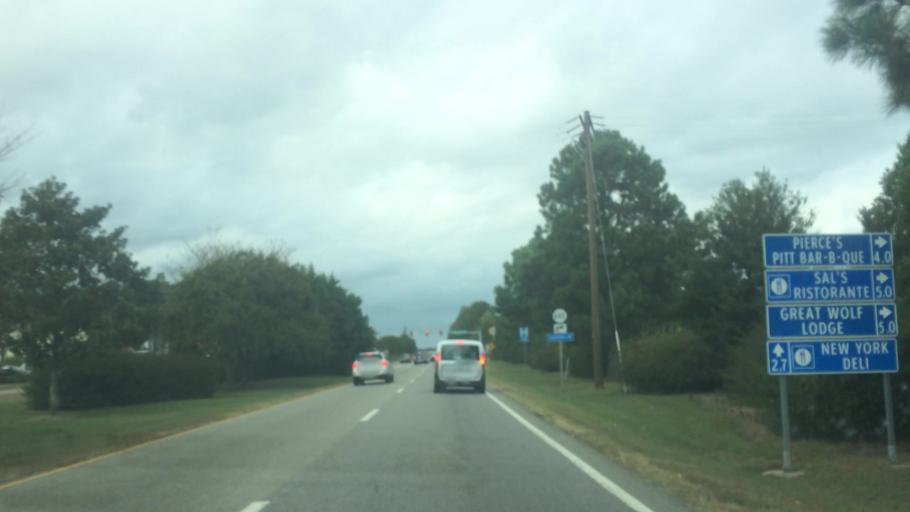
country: US
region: Virginia
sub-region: James City County
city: Williamsburg
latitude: 37.3112
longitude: -76.7314
